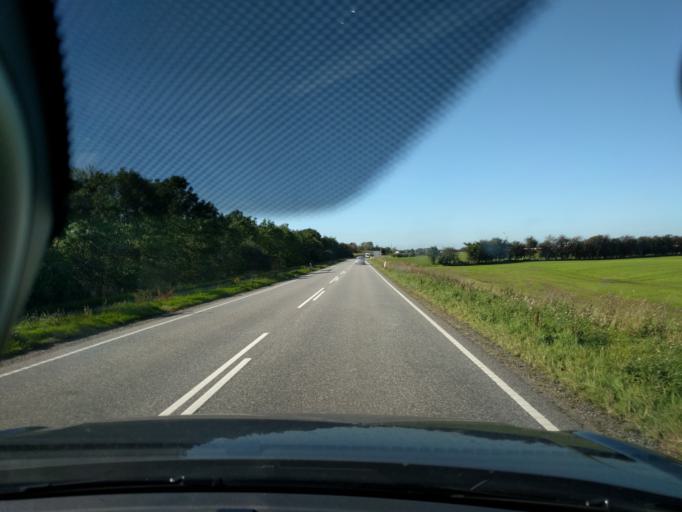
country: DK
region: North Denmark
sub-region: Mariagerfjord Kommune
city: Hobro
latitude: 56.6781
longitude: 9.6677
